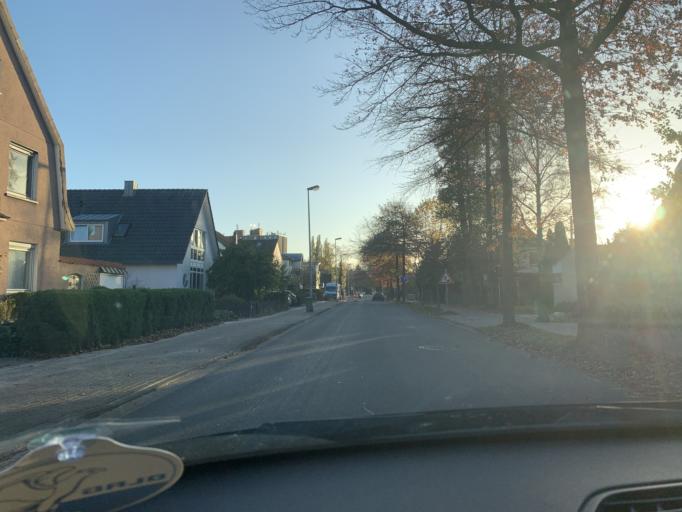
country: DE
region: Lower Saxony
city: Oldenburg
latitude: 53.1433
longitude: 8.1771
